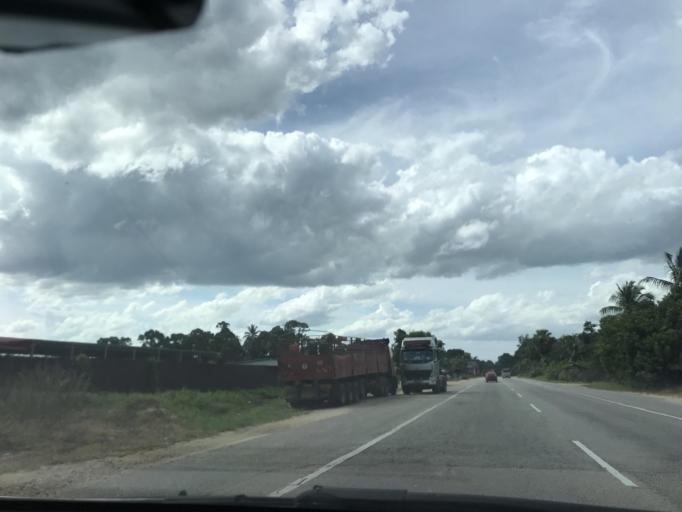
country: MY
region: Kelantan
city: Kampong Pangkal Kalong
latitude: 5.9108
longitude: 102.1876
